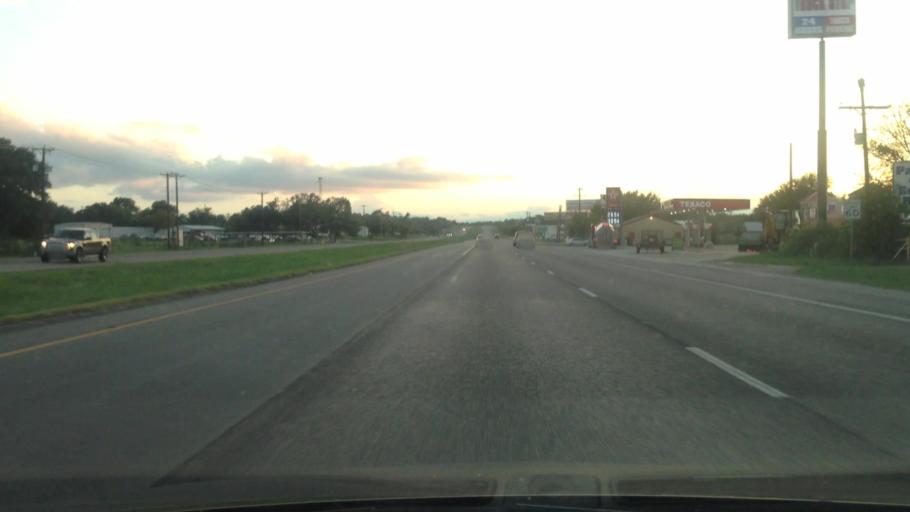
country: US
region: Texas
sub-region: Tarrant County
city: Benbrook
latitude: 32.6163
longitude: -97.5349
